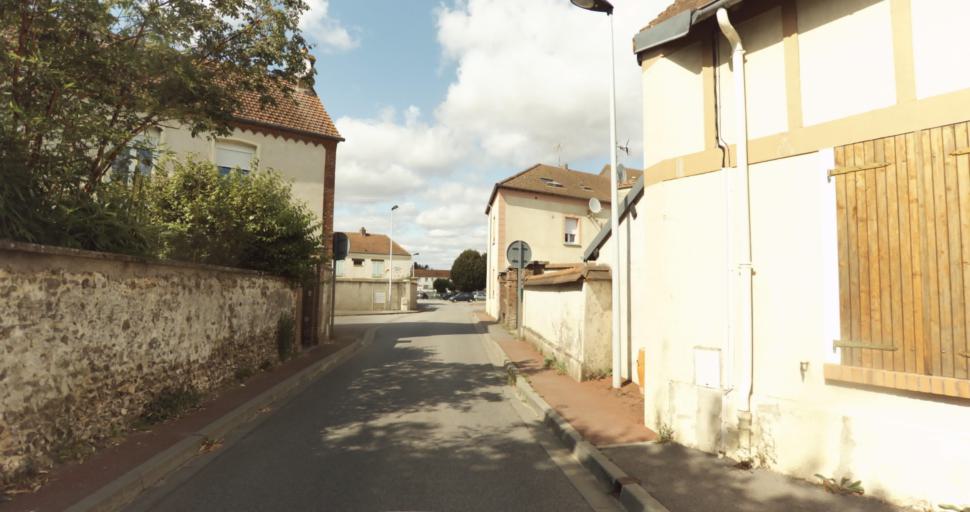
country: FR
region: Haute-Normandie
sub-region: Departement de l'Eure
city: La Couture-Boussey
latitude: 48.8964
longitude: 1.4063
